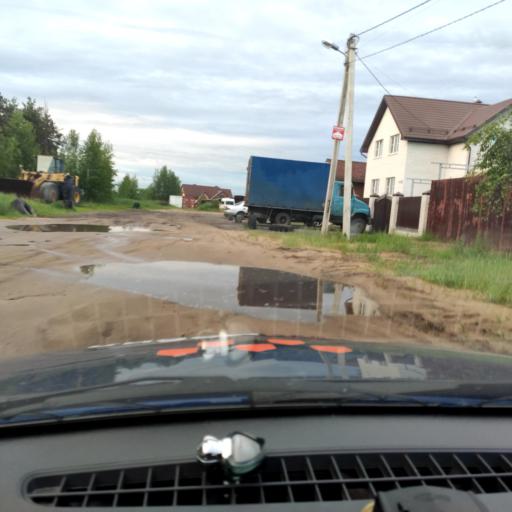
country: RU
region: Voronezj
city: Somovo
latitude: 51.7551
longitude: 39.3224
